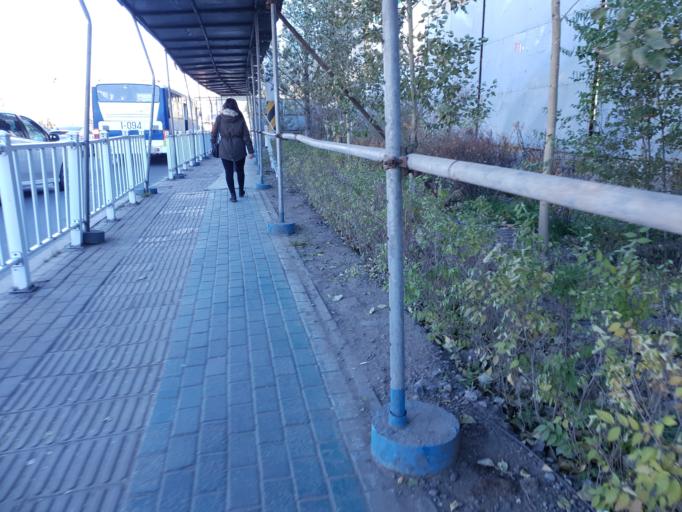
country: MN
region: Ulaanbaatar
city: Ulaanbaatar
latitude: 47.9005
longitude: 106.9100
